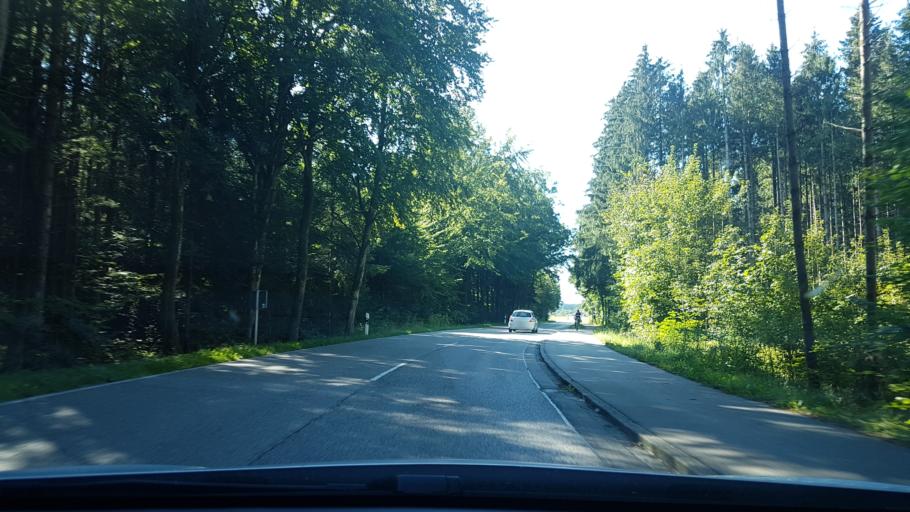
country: DE
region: Bavaria
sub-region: Upper Bavaria
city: Valley
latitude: 47.9182
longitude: 11.7647
